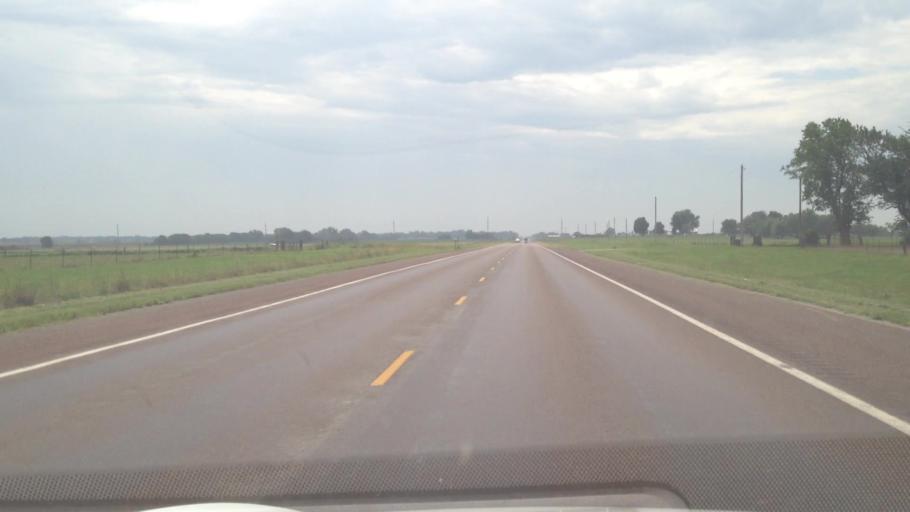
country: US
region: Kansas
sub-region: Crawford County
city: Girard
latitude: 37.4634
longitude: -94.8331
